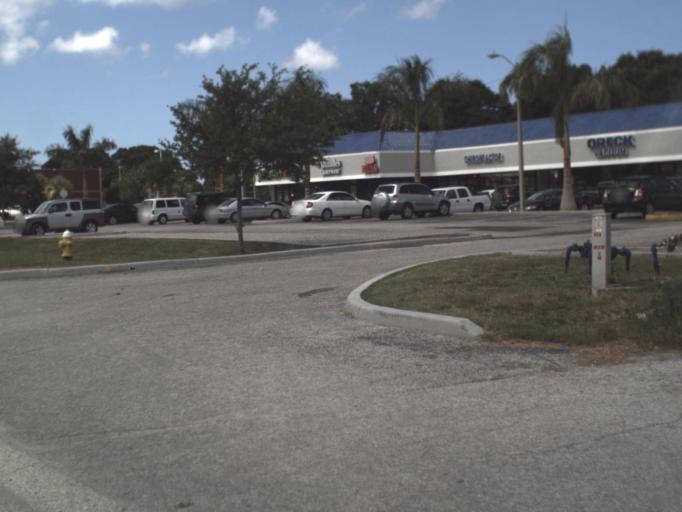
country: US
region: Florida
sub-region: Pinellas County
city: Largo
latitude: 27.8919
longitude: -82.7872
